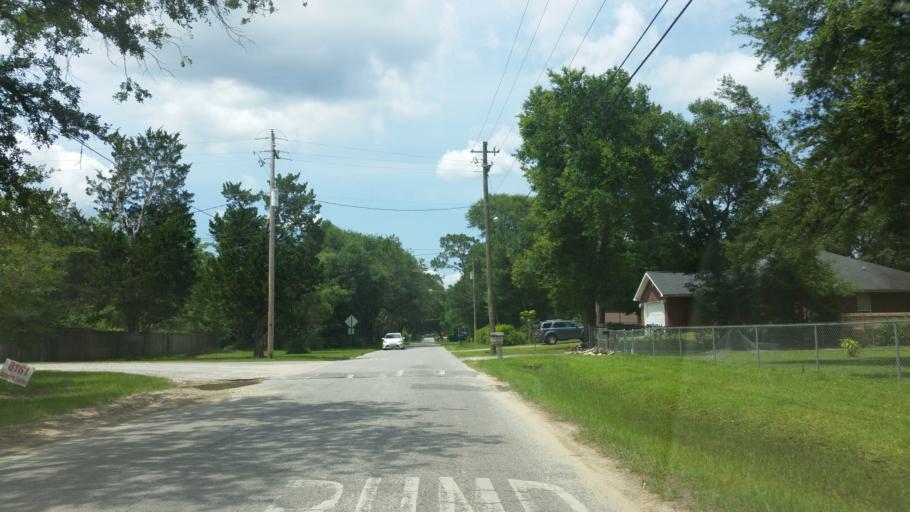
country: US
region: Florida
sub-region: Escambia County
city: Ensley
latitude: 30.5116
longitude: -87.2544
